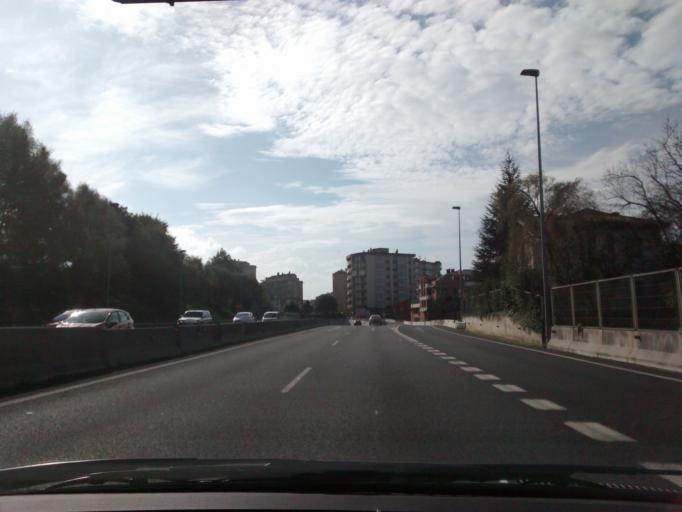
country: ES
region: Cantabria
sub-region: Provincia de Cantabria
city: El Astillero
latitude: 43.4204
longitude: -3.8382
